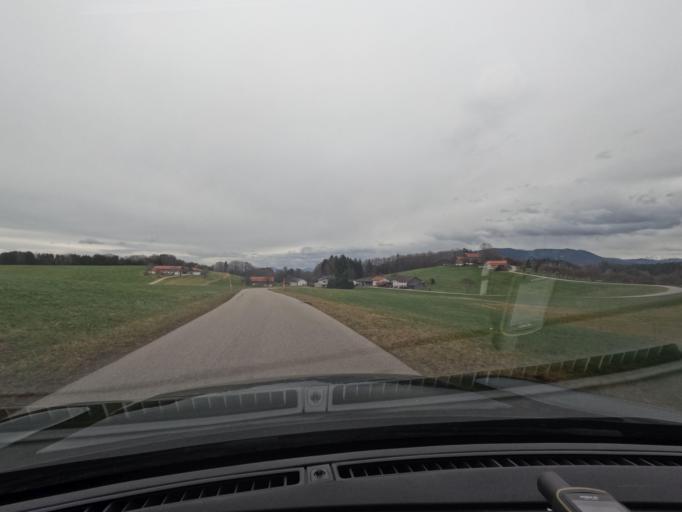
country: DE
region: Bavaria
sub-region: Upper Bavaria
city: Surberg
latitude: 47.8670
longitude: 12.6907
